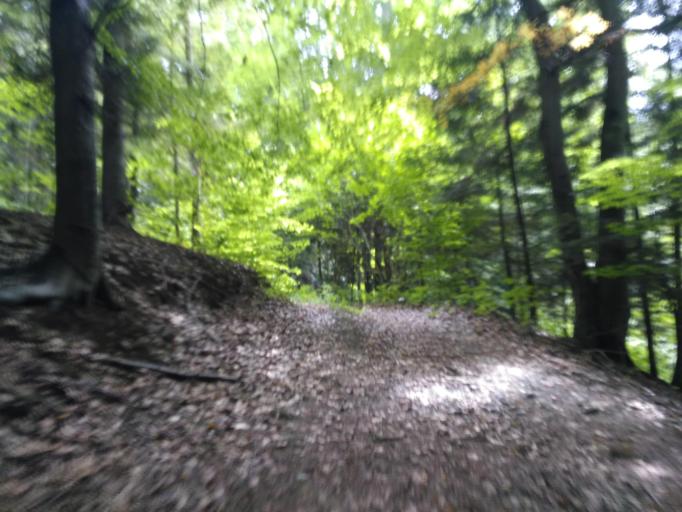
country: PL
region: Subcarpathian Voivodeship
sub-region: Powiat strzyzowski
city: Frysztak
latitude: 49.8879
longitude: 21.5523
